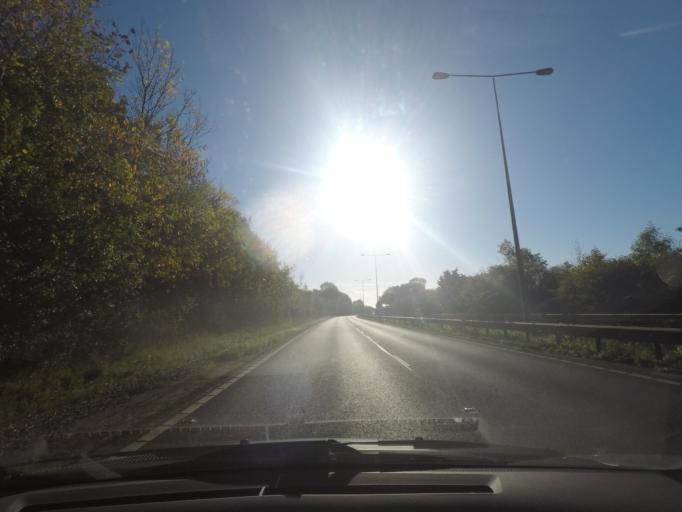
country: GB
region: England
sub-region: East Riding of Yorkshire
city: Brantingham
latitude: 53.7447
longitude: -0.5689
